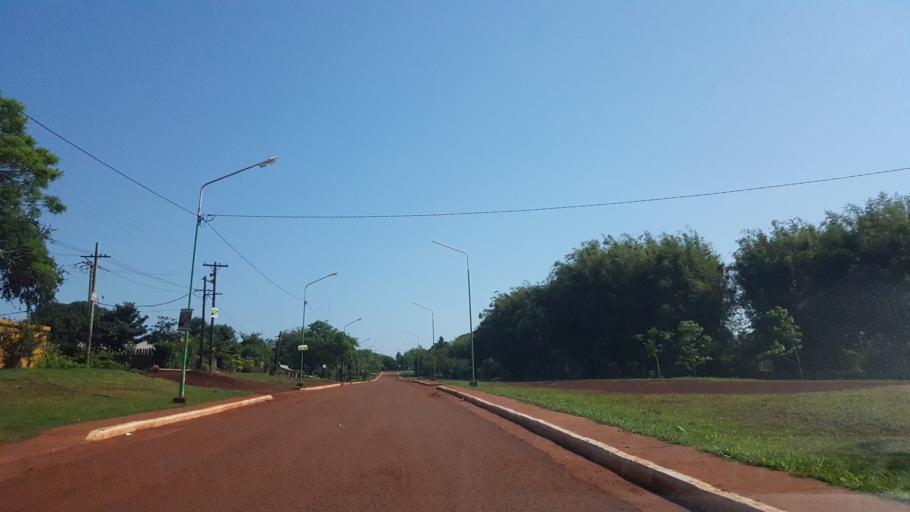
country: AR
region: Corrientes
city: San Carlos
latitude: -27.7510
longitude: -55.8879
